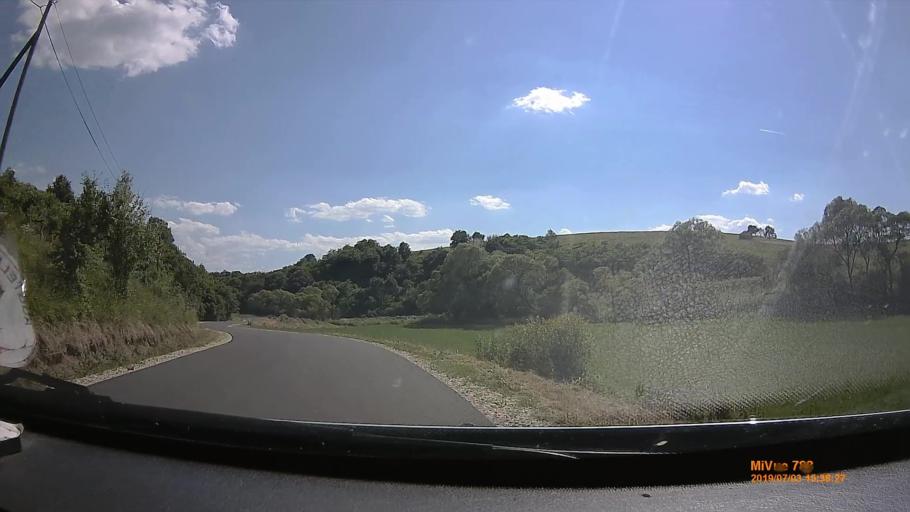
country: HU
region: Heves
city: Szilvasvarad
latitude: 48.1705
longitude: 20.3982
